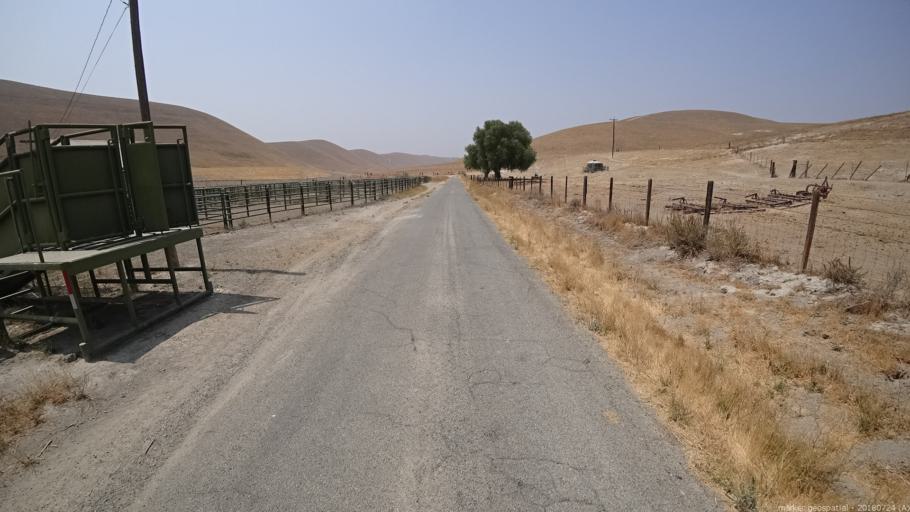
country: US
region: California
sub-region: Monterey County
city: King City
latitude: 36.1918
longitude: -120.9638
